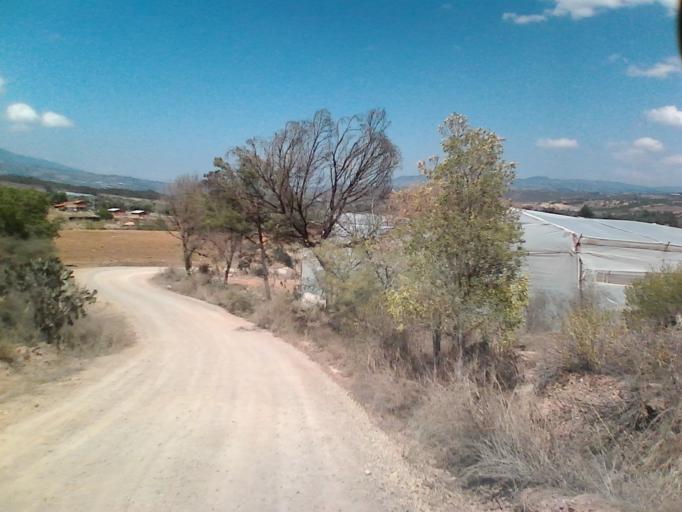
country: CO
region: Boyaca
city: Sachica
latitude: 5.6042
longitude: -73.5610
